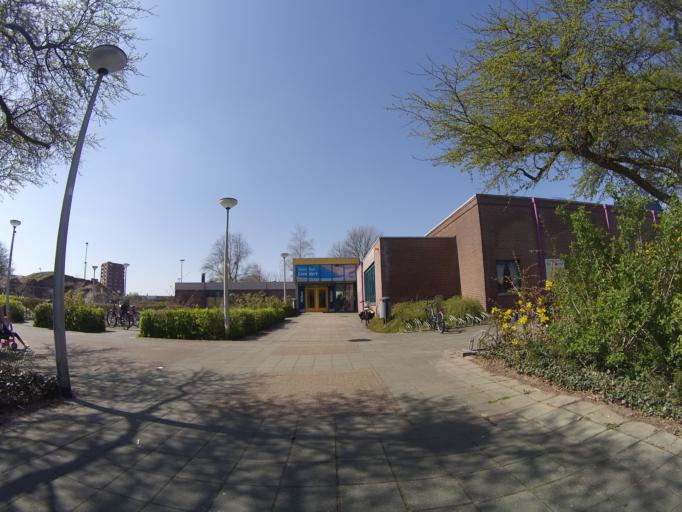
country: NL
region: Utrecht
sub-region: Gemeente Amersfoort
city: Amersfoort
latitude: 52.1680
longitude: 5.3977
